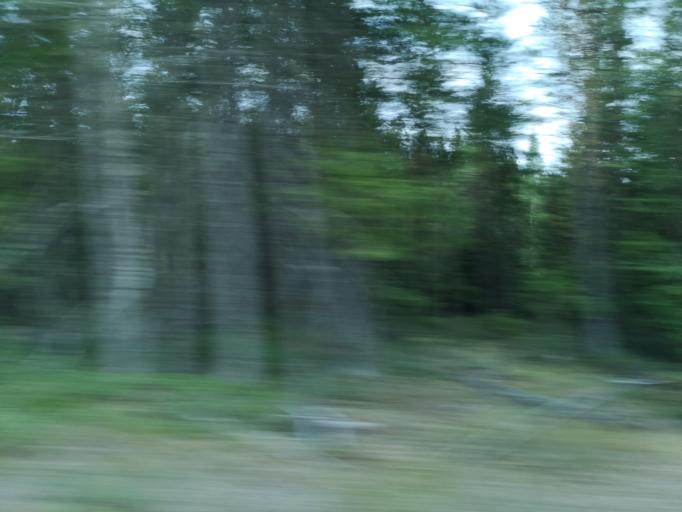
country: FI
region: Central Finland
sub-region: Jyvaeskylae
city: Toivakka
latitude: 62.0874
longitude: 26.0647
